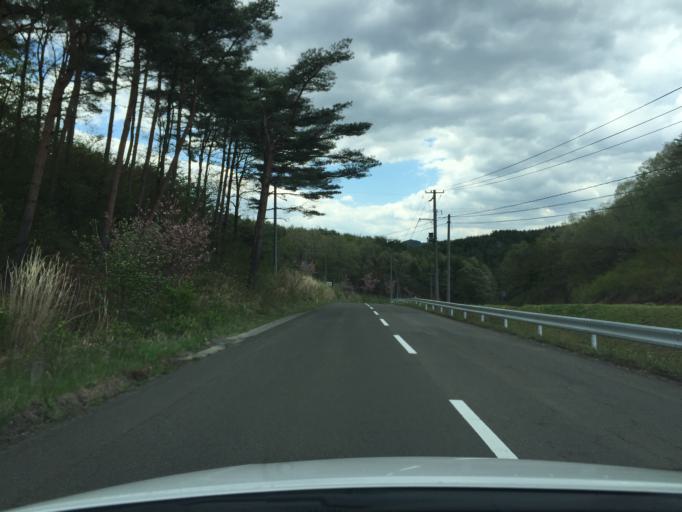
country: JP
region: Fukushima
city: Yanagawamachi-saiwaicho
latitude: 37.7294
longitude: 140.6781
